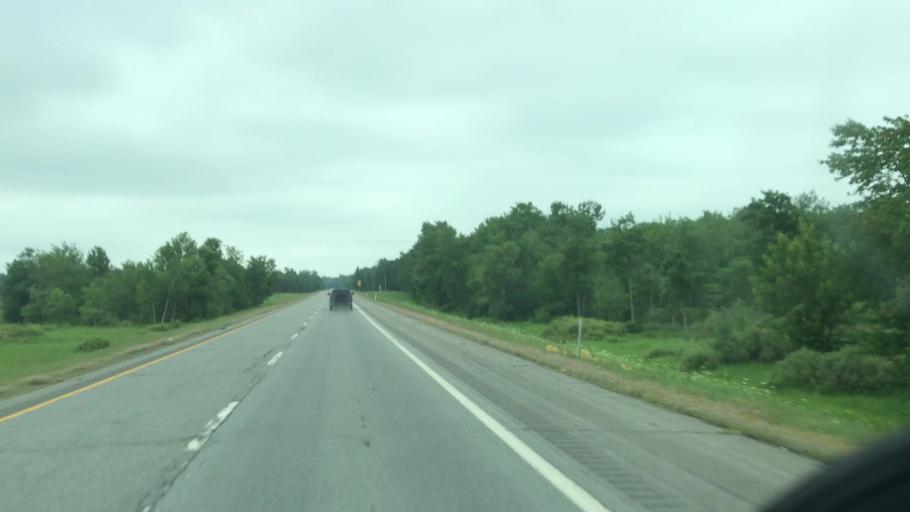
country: US
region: Maine
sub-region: Penobscot County
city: Old Town
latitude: 44.9460
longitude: -68.7078
